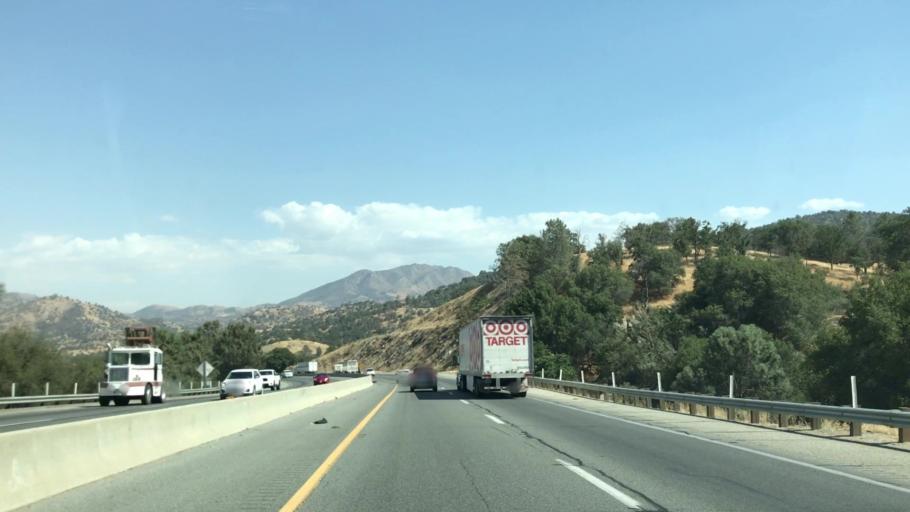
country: US
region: California
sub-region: Kern County
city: Bear Valley Springs
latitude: 35.2468
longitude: -118.5937
